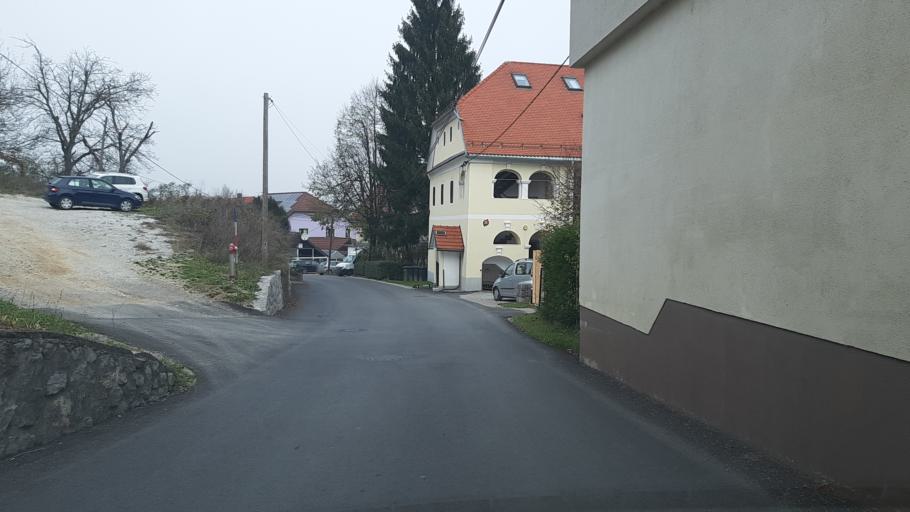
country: SI
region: Borovnica
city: Borovnica
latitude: 45.9154
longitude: 14.3653
